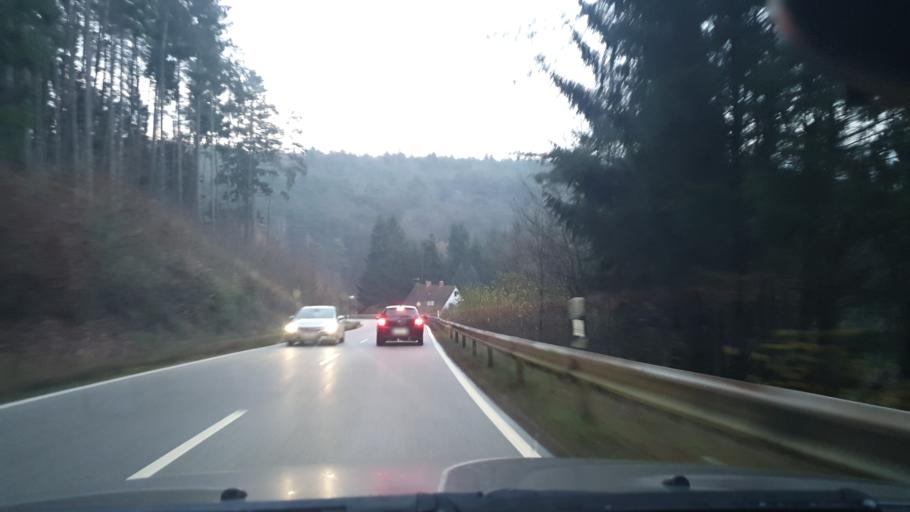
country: DE
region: Rheinland-Pfalz
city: Krickenbach
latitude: 49.3908
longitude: 7.6903
